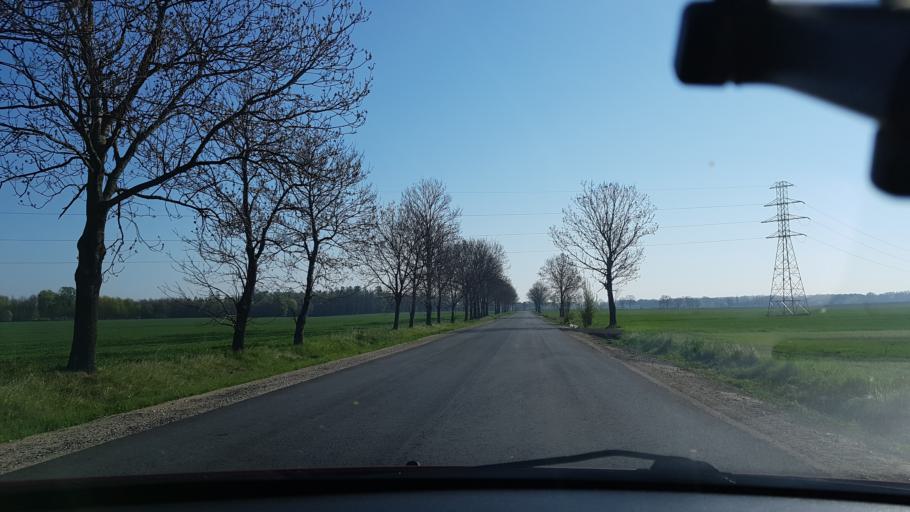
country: CZ
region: Olomoucky
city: Vidnava
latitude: 50.4241
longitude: 17.2340
